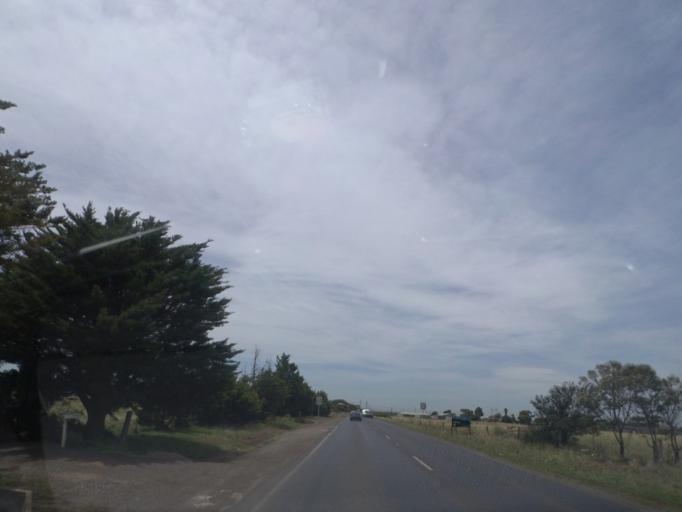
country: AU
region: Victoria
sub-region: Melton
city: Rockbank
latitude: -37.7410
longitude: 144.7017
